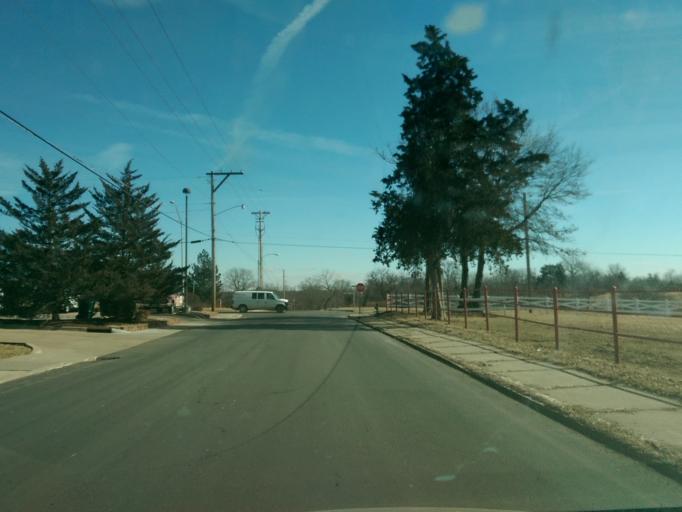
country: US
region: Missouri
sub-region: Boone County
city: Columbia
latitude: 38.9567
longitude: -92.3129
